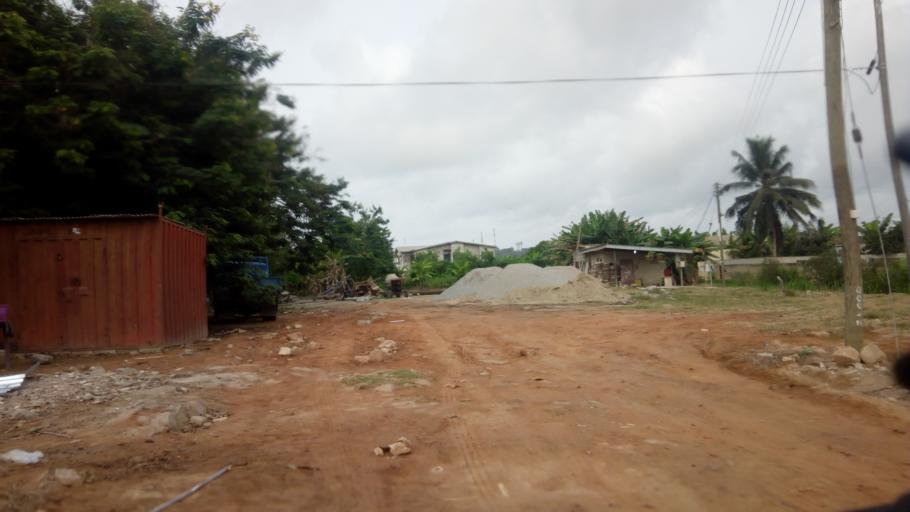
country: GH
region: Central
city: Cape Coast
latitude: 5.1219
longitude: -1.2746
